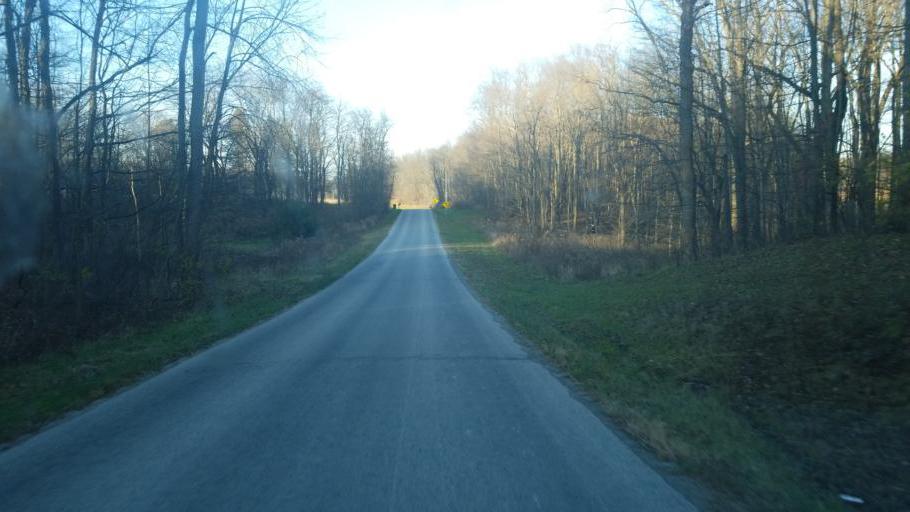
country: US
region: Ohio
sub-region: Richland County
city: Ontario
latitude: 40.7183
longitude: -82.6565
